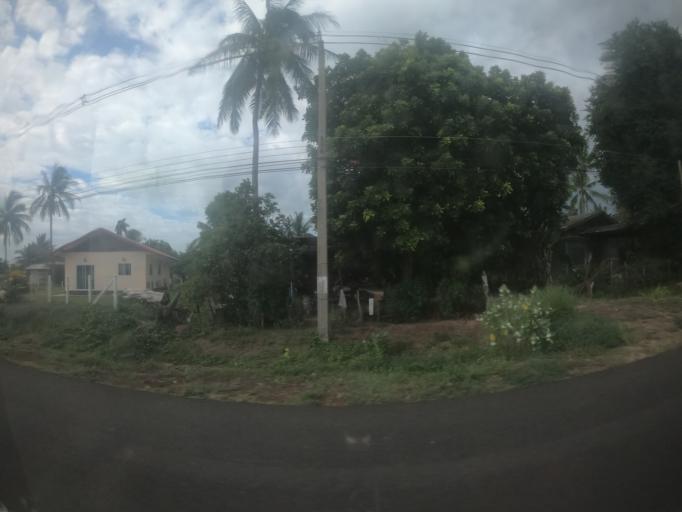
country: TH
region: Surin
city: Prasat
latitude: 14.5642
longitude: 103.4949
